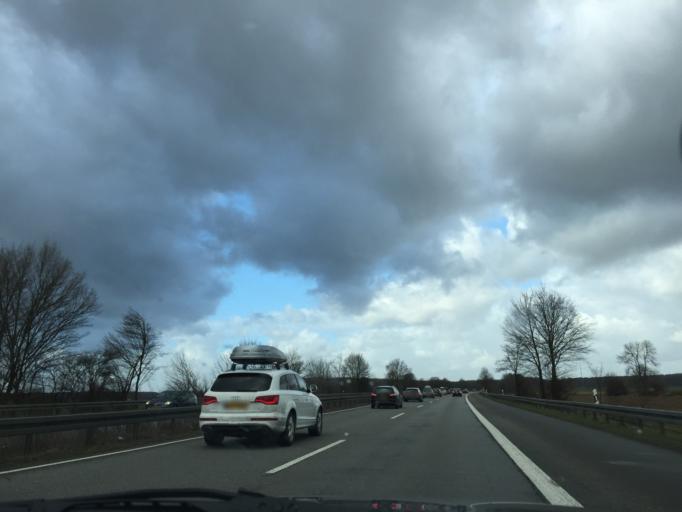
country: DE
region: North Rhine-Westphalia
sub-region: Regierungsbezirk Dusseldorf
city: Emmerich
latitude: 51.8654
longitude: 6.2229
